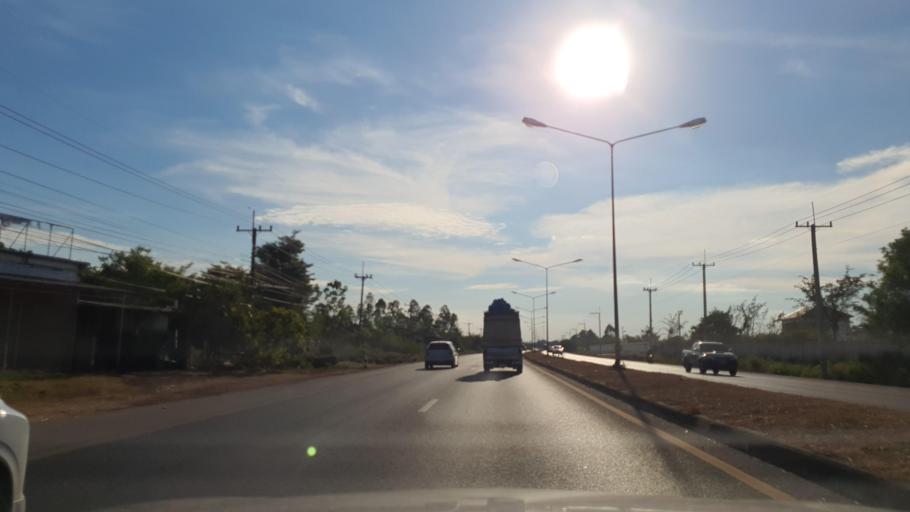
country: TH
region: Maha Sarakham
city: Kantharawichai
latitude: 16.3560
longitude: 103.3329
